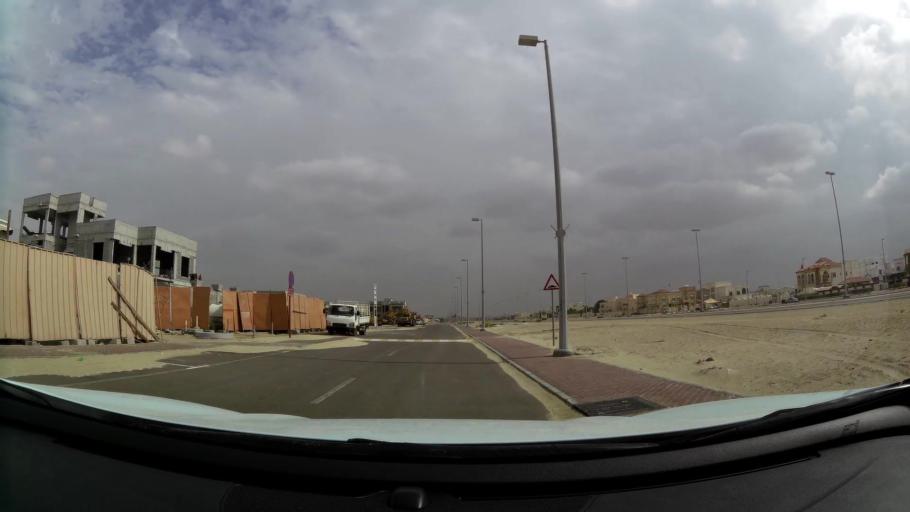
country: AE
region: Abu Dhabi
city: Abu Dhabi
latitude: 24.3808
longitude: 54.6388
